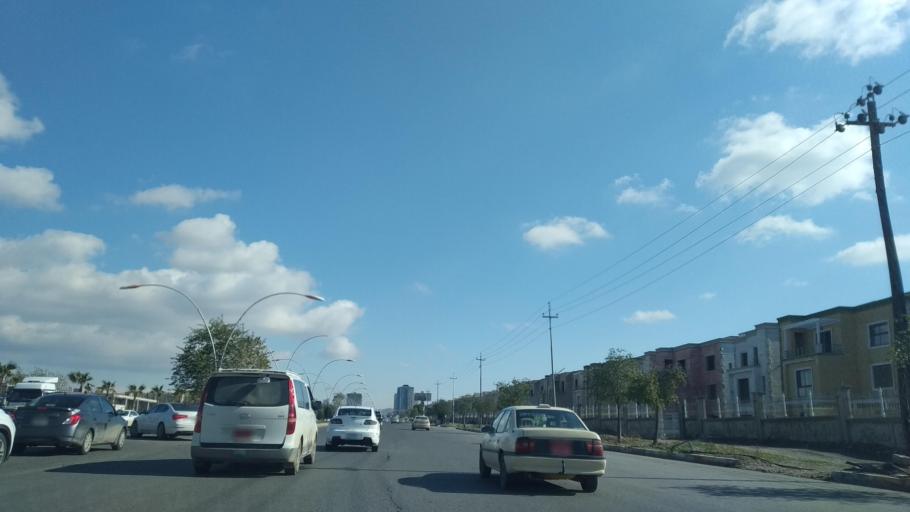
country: IQ
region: Arbil
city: Erbil
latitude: 36.2023
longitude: 44.1039
